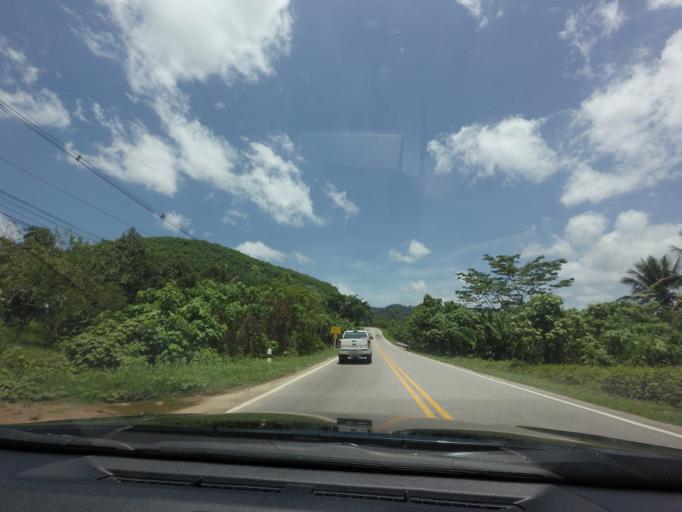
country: TH
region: Chumphon
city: Ban Nam Yuen
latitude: 9.9097
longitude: 98.9355
